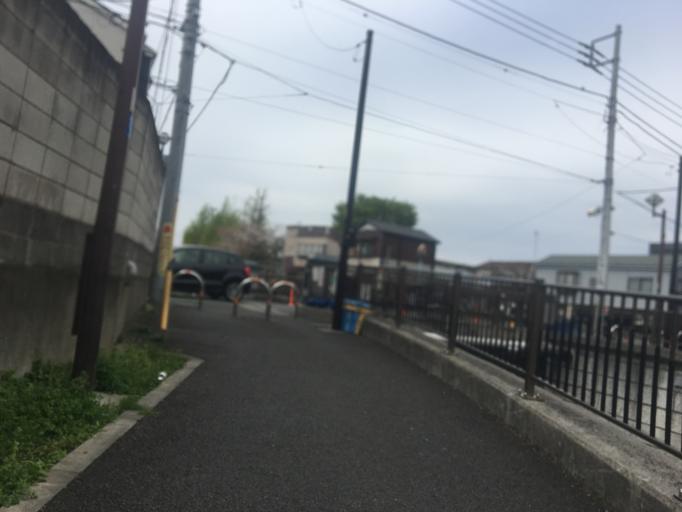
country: JP
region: Tokyo
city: Tokyo
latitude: 35.6809
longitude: 139.6539
